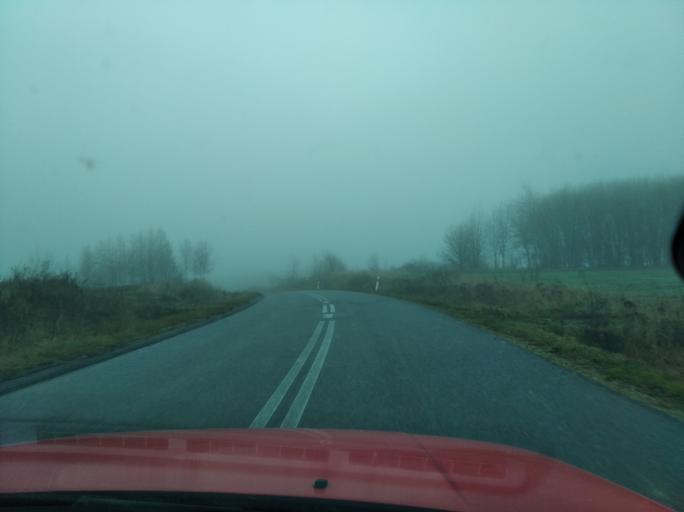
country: PL
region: Subcarpathian Voivodeship
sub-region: Powiat jaroslawski
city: Jodlowka
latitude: 49.8825
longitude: 22.4655
